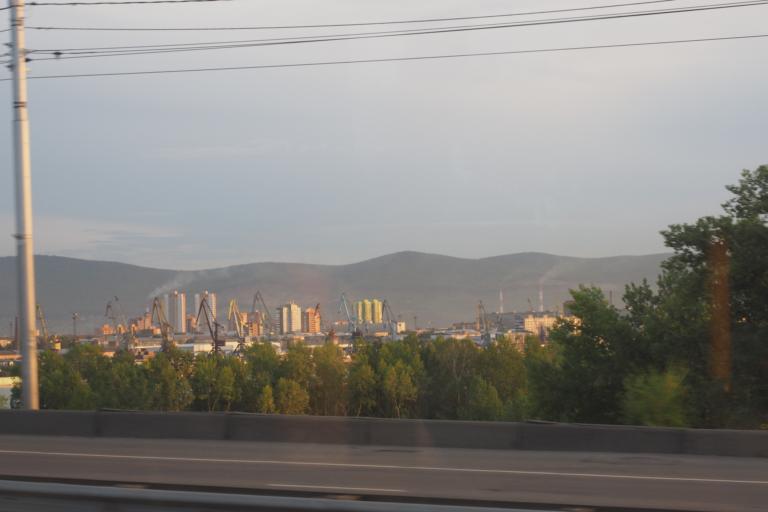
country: RU
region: Krasnoyarskiy
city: Krasnoyarsk
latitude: 56.0225
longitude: 92.9454
